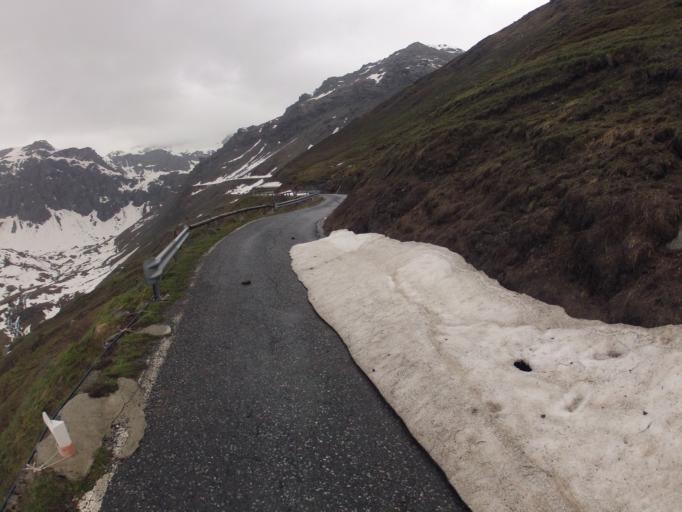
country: IT
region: Piedmont
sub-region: Provincia di Cuneo
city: Crissolo
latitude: 44.7037
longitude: 7.1153
